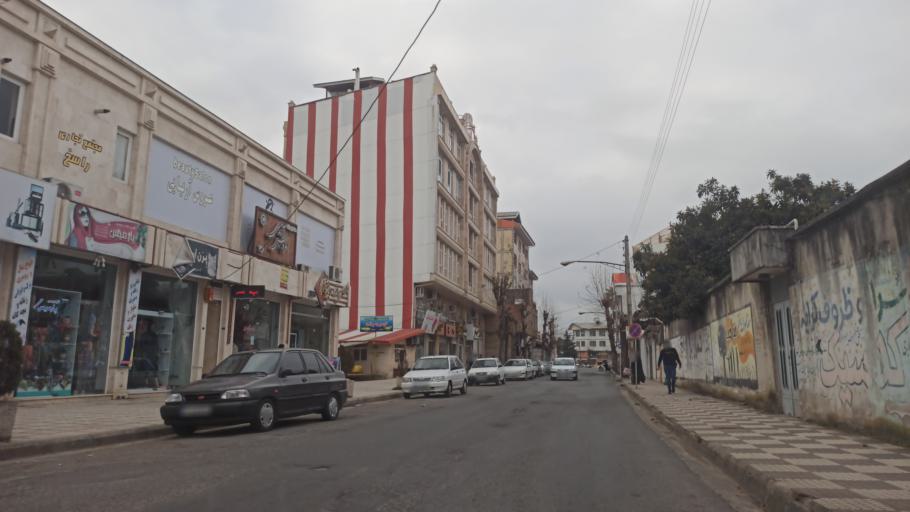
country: IR
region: Gilan
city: Fuman
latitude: 37.2298
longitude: 49.3163
